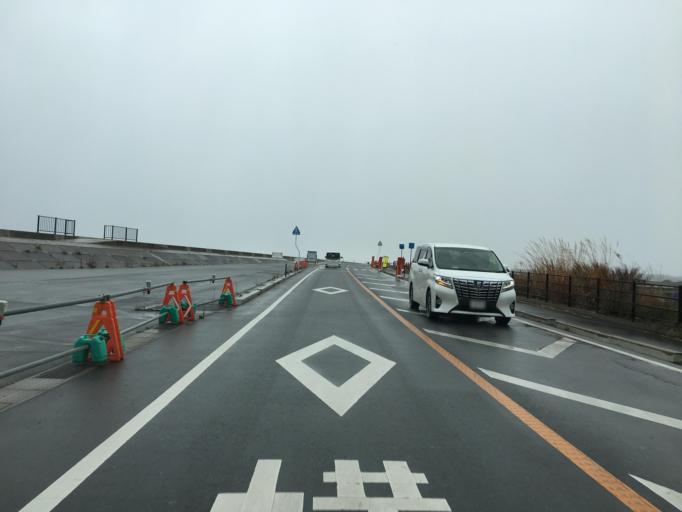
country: JP
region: Miyagi
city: Marumori
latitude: 37.8257
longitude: 140.9858
